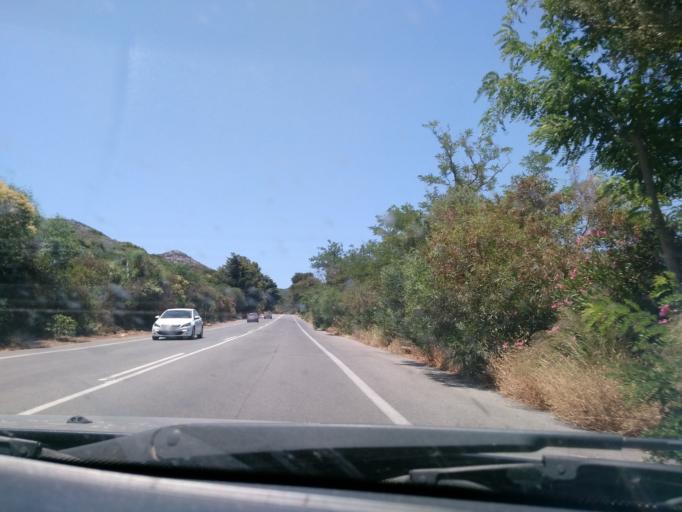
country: GR
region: Crete
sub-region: Nomos Rethymnis
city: Anogeia
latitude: 35.3996
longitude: 24.8746
